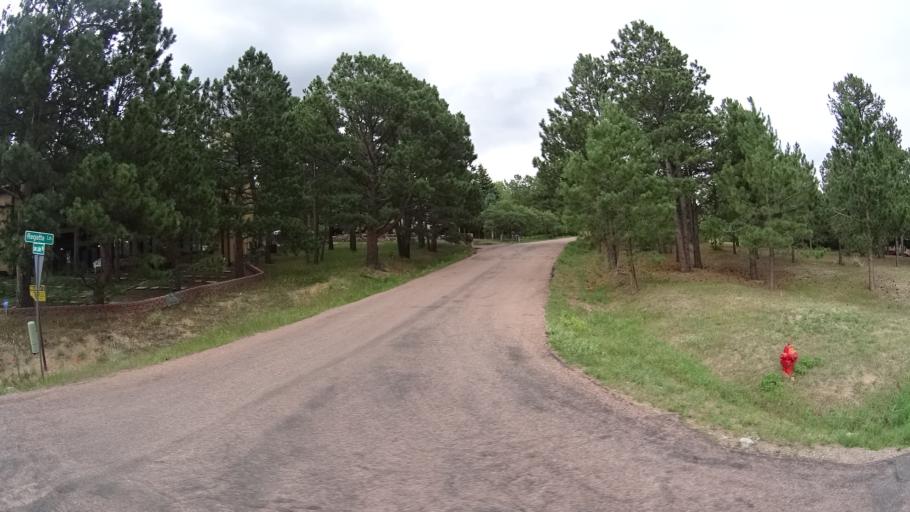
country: US
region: Colorado
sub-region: El Paso County
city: Woodmoor
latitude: 39.1017
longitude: -104.8538
